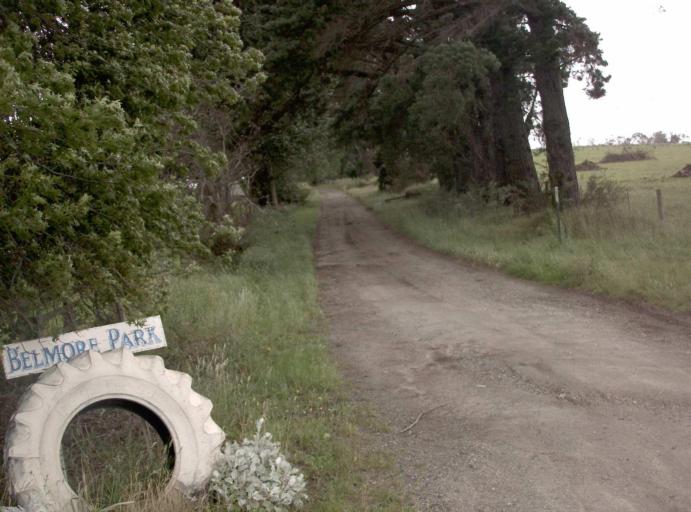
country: AU
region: Victoria
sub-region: Baw Baw
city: Warragul
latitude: -38.0943
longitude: 145.8517
